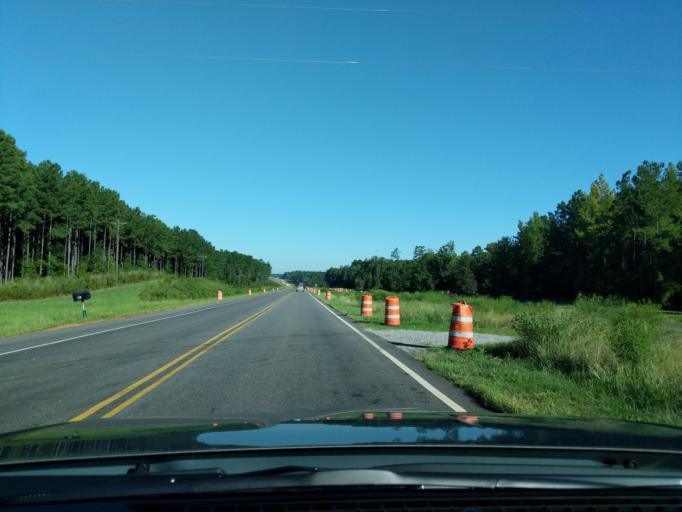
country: US
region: Georgia
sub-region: McDuffie County
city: Thomson
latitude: 33.5756
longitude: -82.5229
